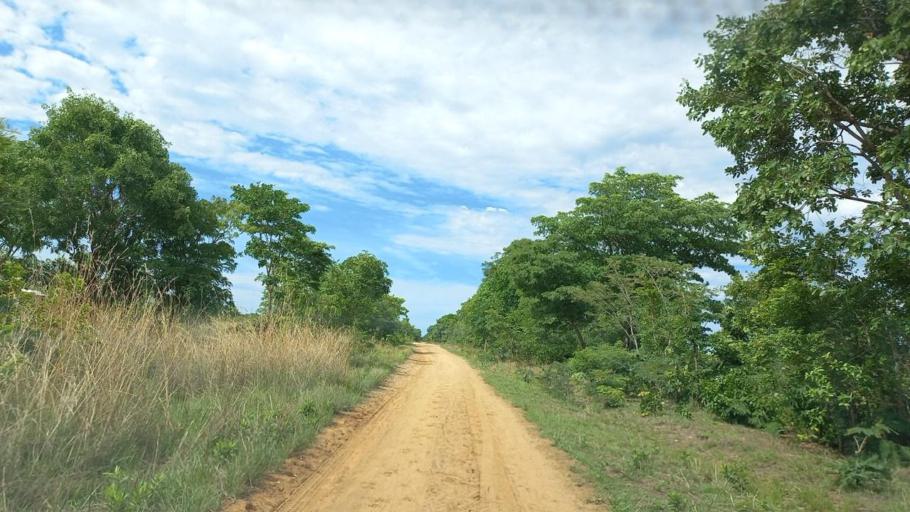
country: ZM
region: North-Western
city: Kabompo
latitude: -13.5169
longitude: 24.3881
